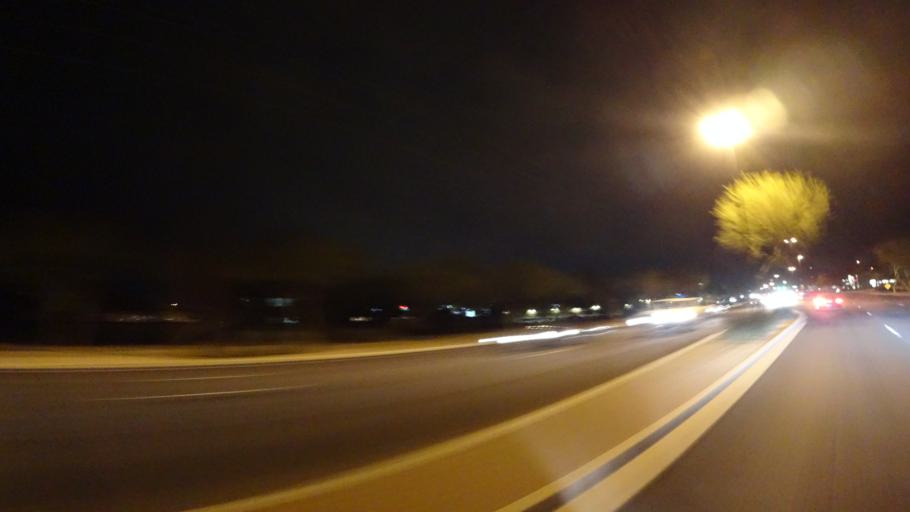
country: US
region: Arizona
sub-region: Maricopa County
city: Queen Creek
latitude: 33.2307
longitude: -111.7208
